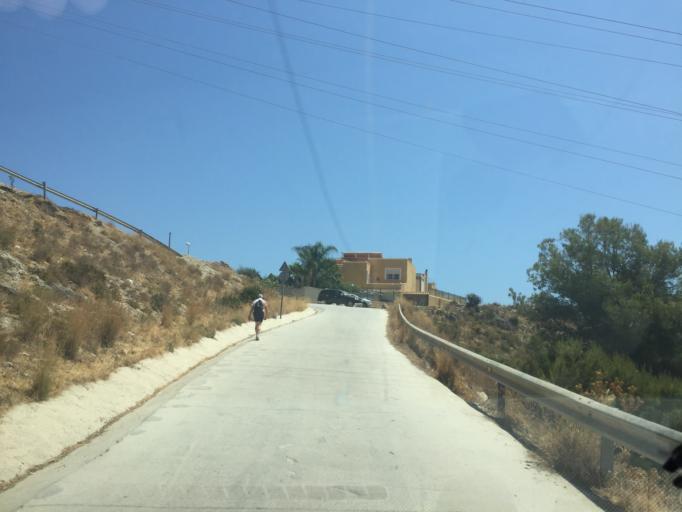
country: ES
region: Andalusia
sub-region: Provincia de Malaga
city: Nerja
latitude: 36.7645
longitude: -3.8746
